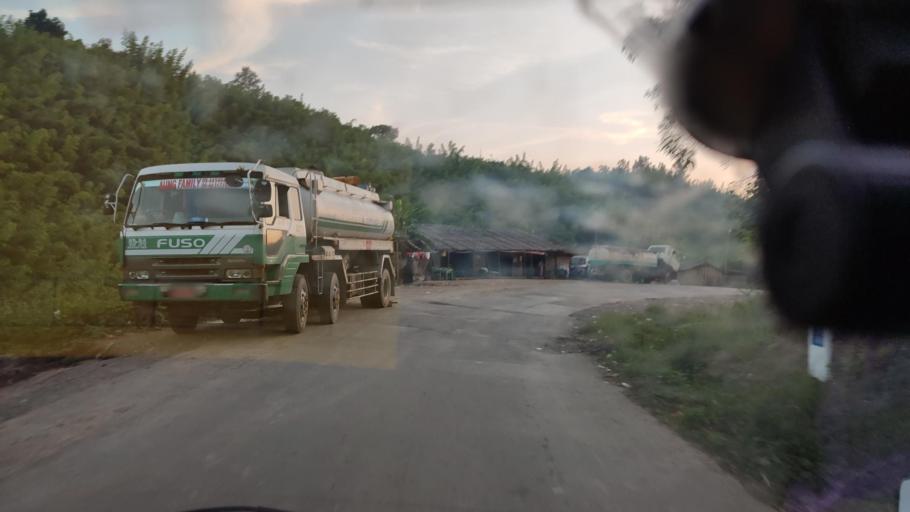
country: MM
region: Magway
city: Minbu
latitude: 19.8078
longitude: 94.0654
